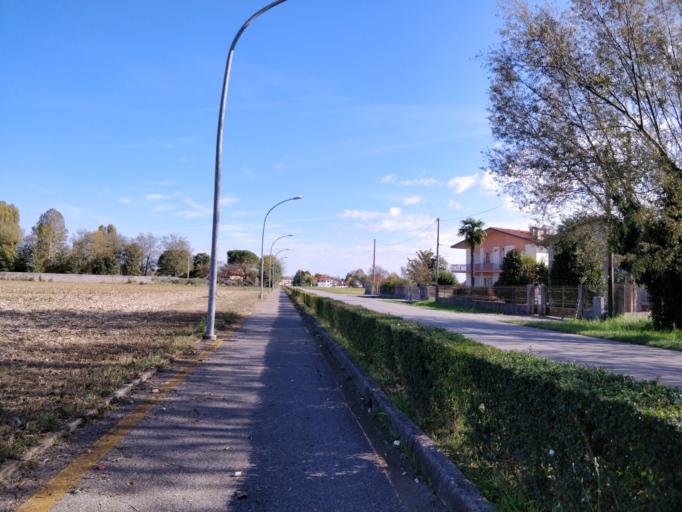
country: IT
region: Friuli Venezia Giulia
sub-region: Provincia di Udine
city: Codroipo
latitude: 45.9473
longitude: 13.0158
